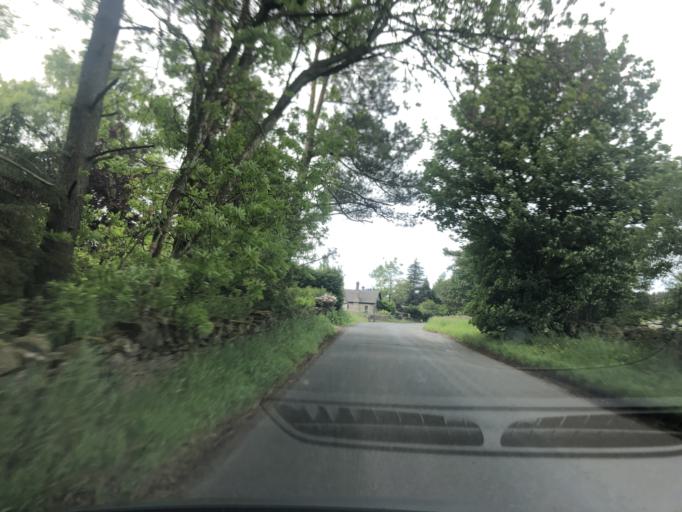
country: GB
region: Scotland
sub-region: The Scottish Borders
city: West Linton
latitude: 55.7344
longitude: -3.3308
